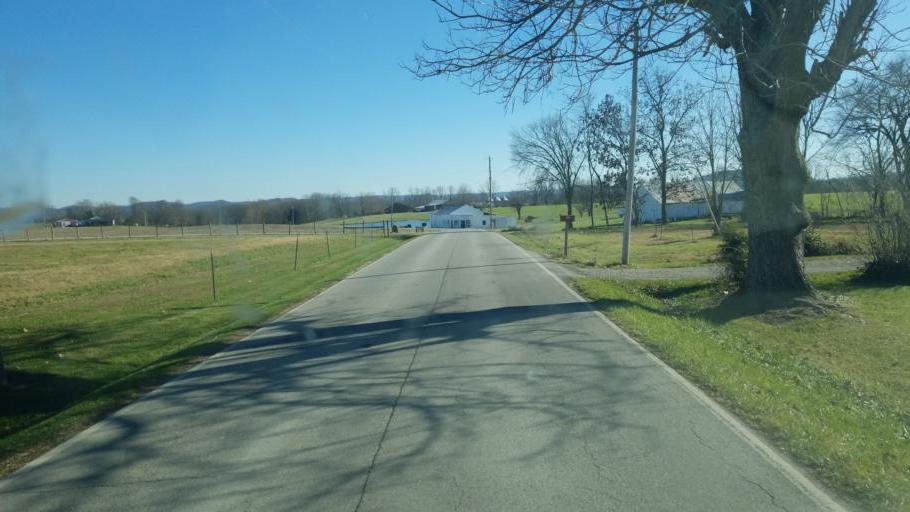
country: US
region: Ohio
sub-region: Adams County
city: Manchester
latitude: 38.5349
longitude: -83.6280
